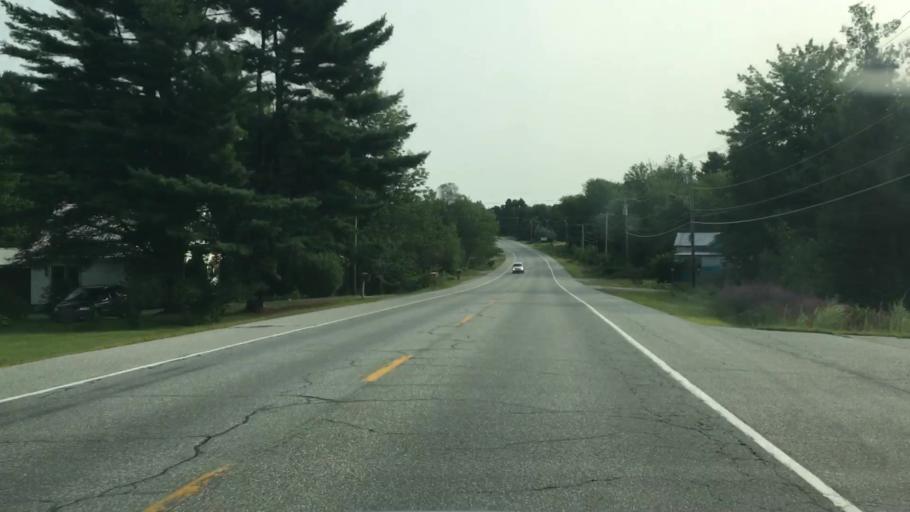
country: US
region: Maine
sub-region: Kennebec County
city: Gardiner
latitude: 44.1880
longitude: -69.8170
